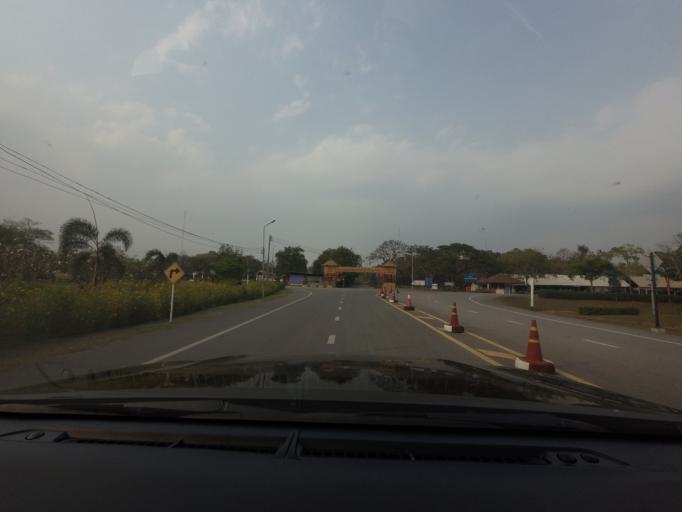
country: TH
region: Sara Buri
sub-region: Amphoe Wang Muang
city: Wang Muang
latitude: 14.8656
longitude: 101.0625
